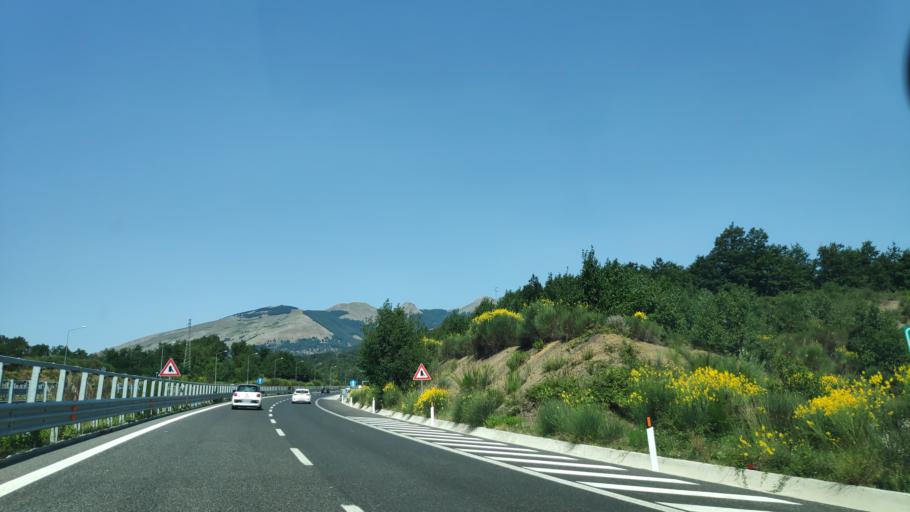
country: IT
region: Basilicate
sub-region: Provincia di Potenza
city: Lauria
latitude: 40.0760
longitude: 15.8577
